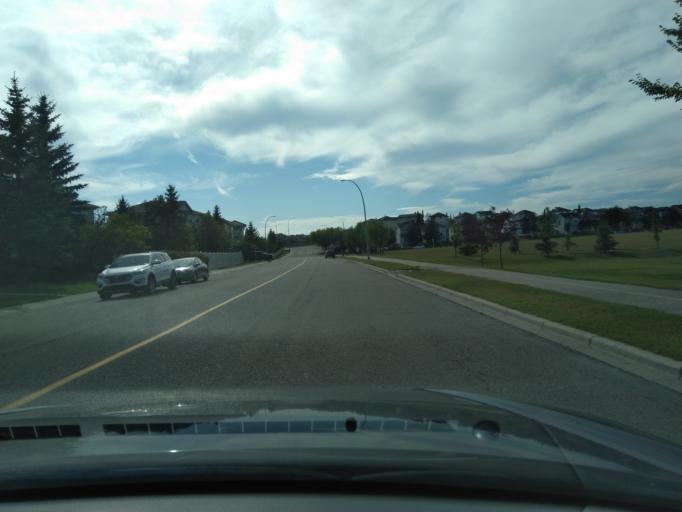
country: CA
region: Alberta
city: Calgary
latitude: 51.1464
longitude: -114.0695
